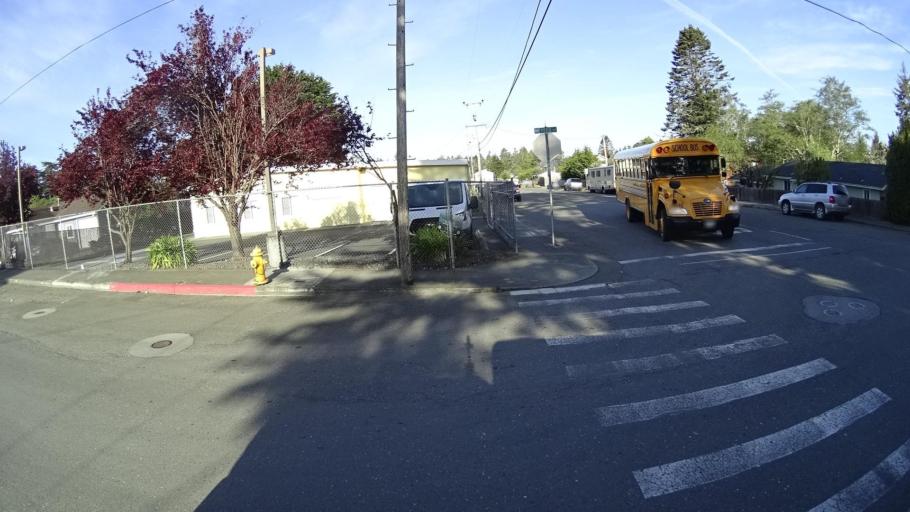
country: US
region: California
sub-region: Humboldt County
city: Bayview
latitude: 40.7654
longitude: -124.1777
